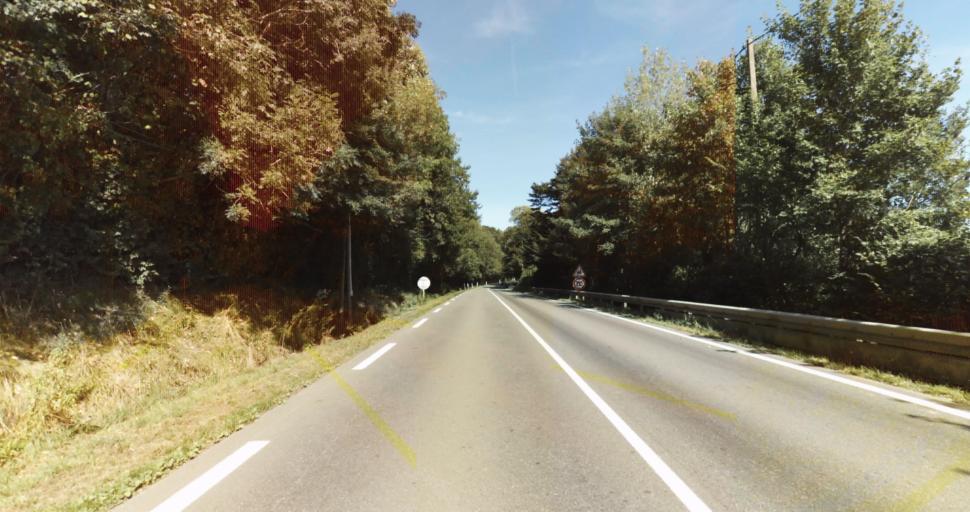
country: FR
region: Lower Normandy
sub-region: Departement de l'Orne
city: Gace
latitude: 48.7325
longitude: 0.2452
